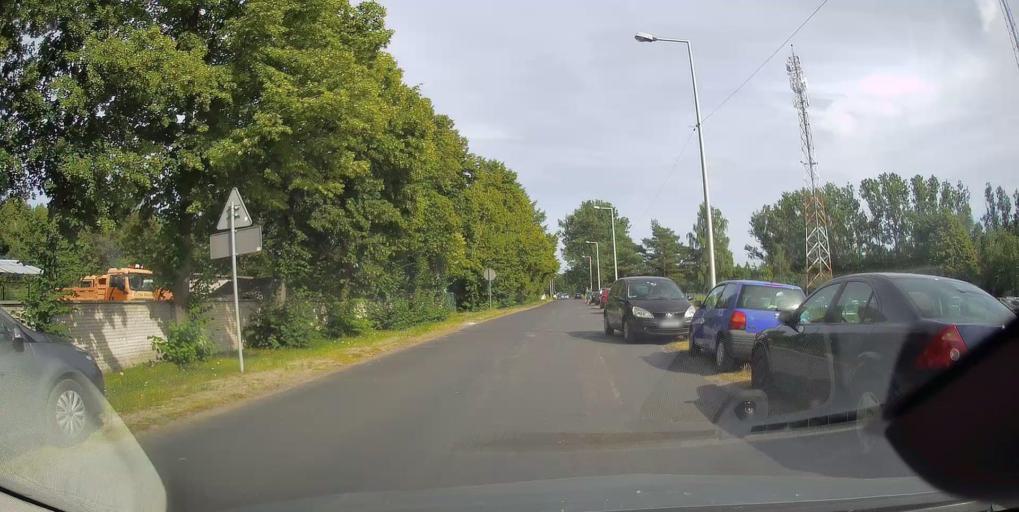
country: PL
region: Lodz Voivodeship
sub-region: Powiat tomaszowski
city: Tomaszow Mazowiecki
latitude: 51.4719
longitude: 20.0135
